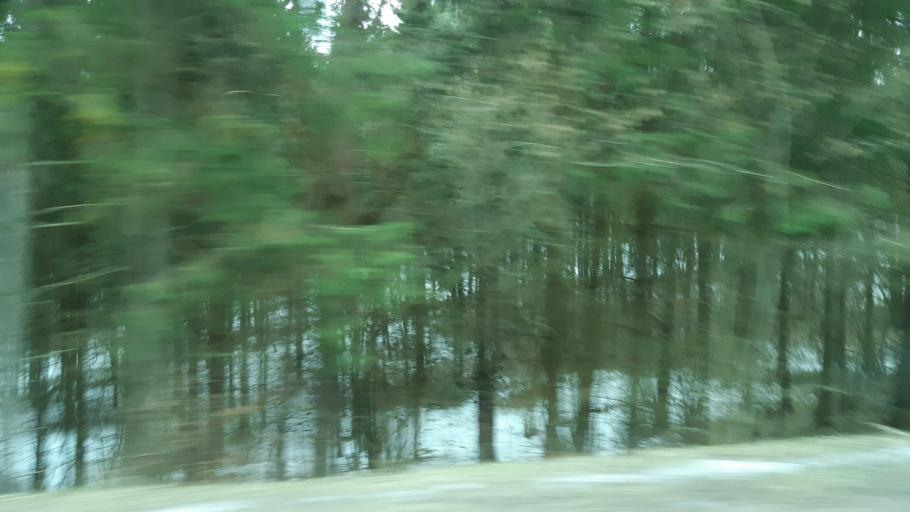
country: PL
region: Podlasie
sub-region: Suwalki
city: Suwalki
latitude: 54.2880
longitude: 22.9542
